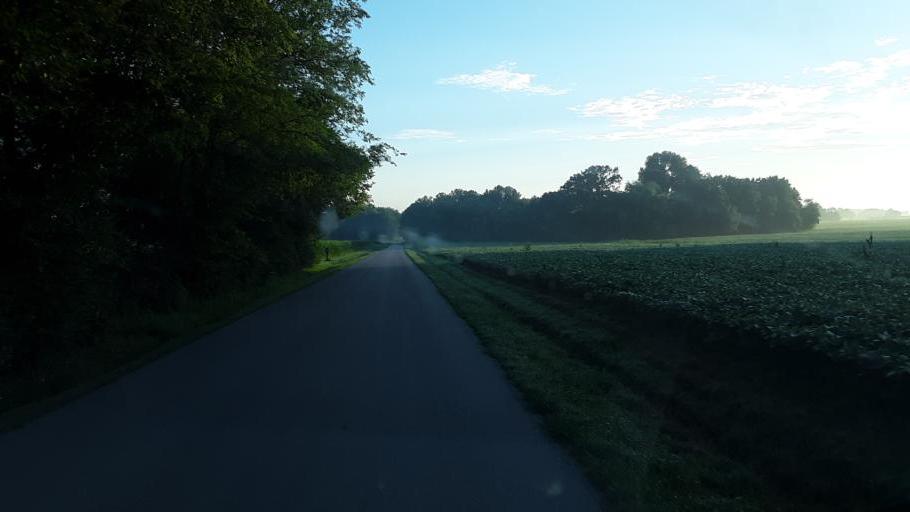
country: US
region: Kentucky
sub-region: Todd County
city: Guthrie
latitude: 36.7263
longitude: -87.1686
